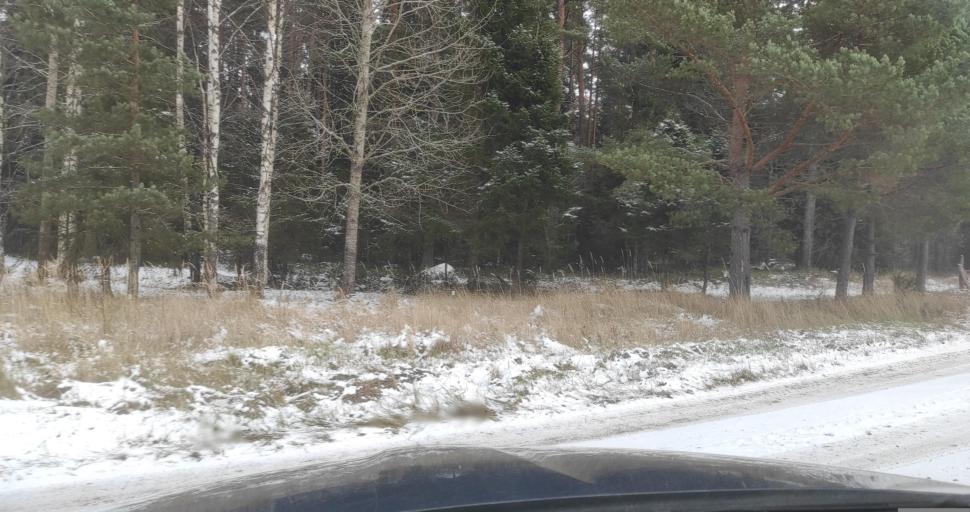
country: LV
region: Kuldigas Rajons
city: Kuldiga
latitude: 56.9940
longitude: 21.8072
